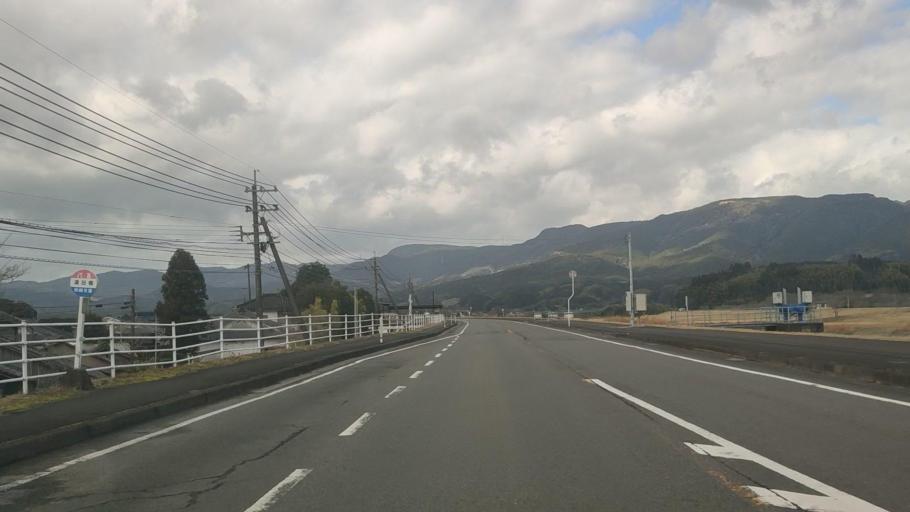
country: JP
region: Kumamoto
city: Hitoyoshi
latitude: 32.0542
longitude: 130.7988
